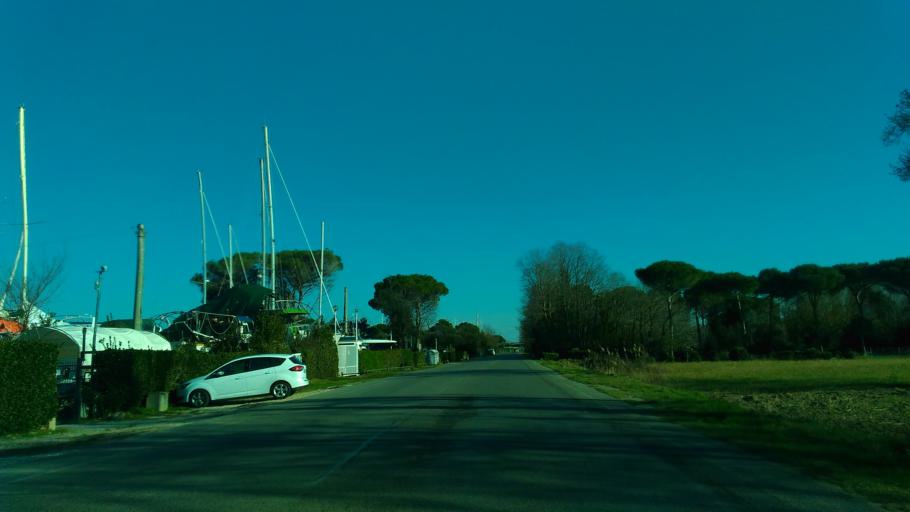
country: IT
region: Tuscany
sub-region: Province of Pisa
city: Marina di Pisa
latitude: 43.6792
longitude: 10.2902
